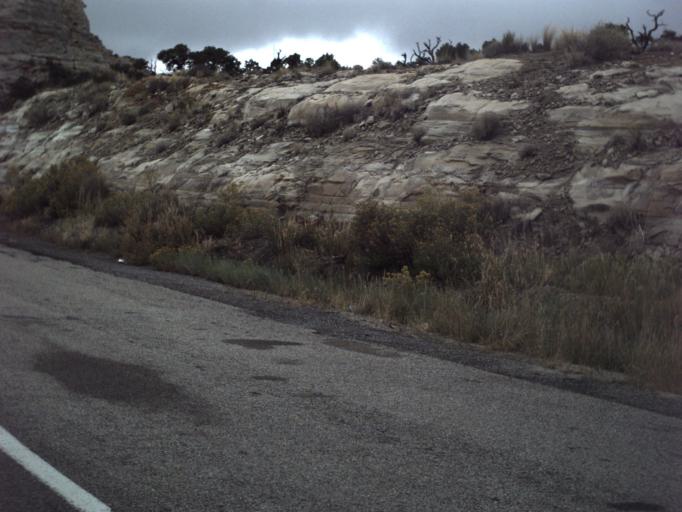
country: US
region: Utah
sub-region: Emery County
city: Ferron
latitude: 38.8625
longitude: -110.8142
